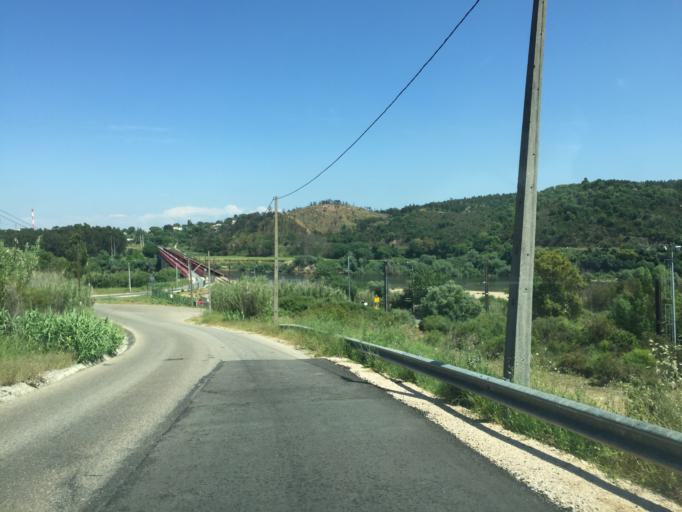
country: PT
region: Santarem
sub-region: Constancia
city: Constancia
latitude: 39.4684
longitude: -8.3459
